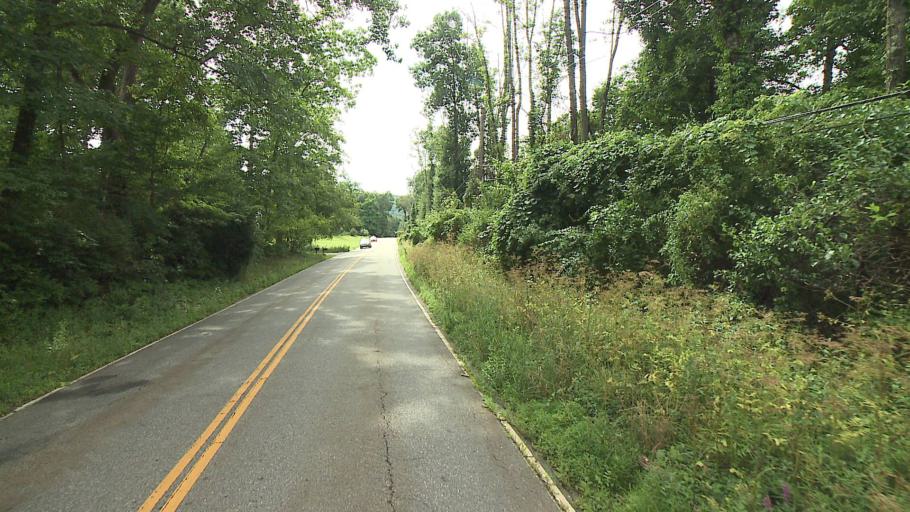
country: US
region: Connecticut
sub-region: Litchfield County
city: Kent
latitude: 41.7447
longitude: -73.5023
